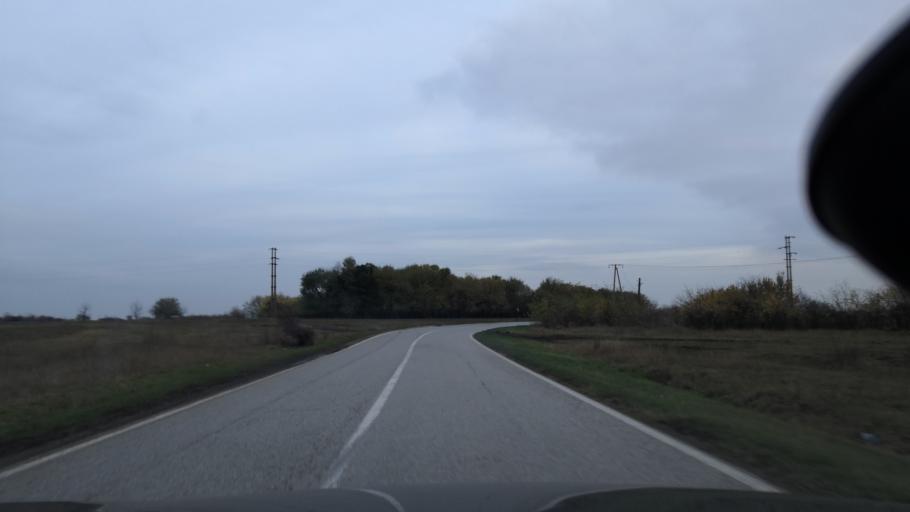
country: RS
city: Sanad
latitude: 45.9758
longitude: 20.1178
